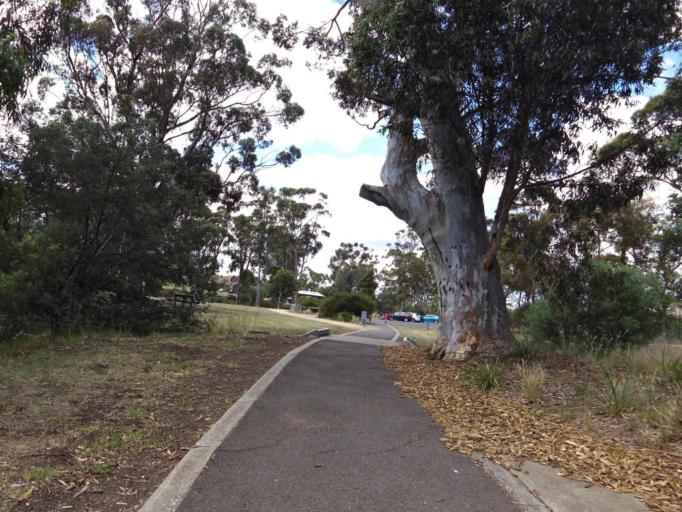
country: AU
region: Victoria
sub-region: Hume
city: Westmeadows
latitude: -37.6750
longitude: 144.8850
